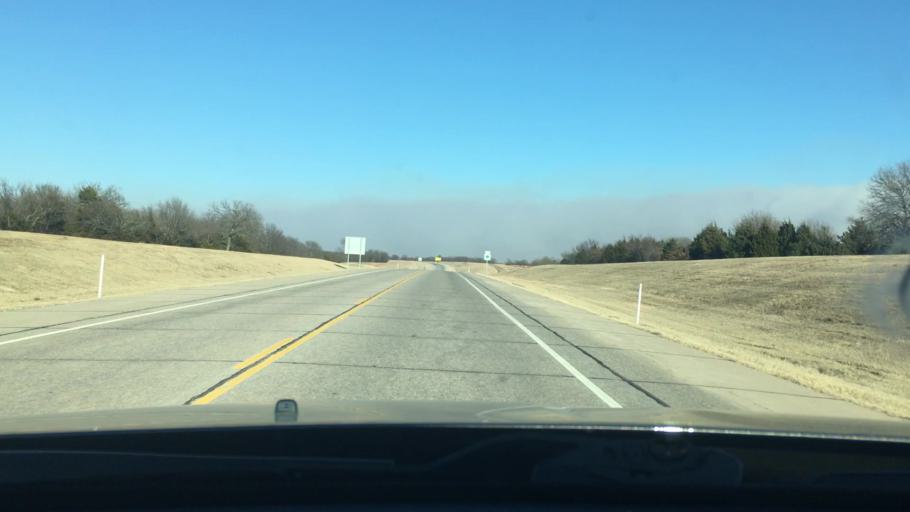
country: US
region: Oklahoma
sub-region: Murray County
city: Sulphur
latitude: 34.5467
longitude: -96.9533
